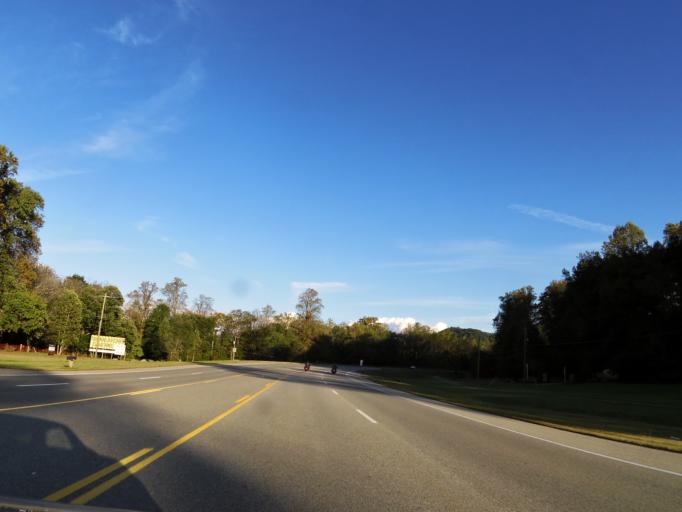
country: US
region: Tennessee
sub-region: Blount County
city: Wildwood
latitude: 35.6795
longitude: -83.7708
